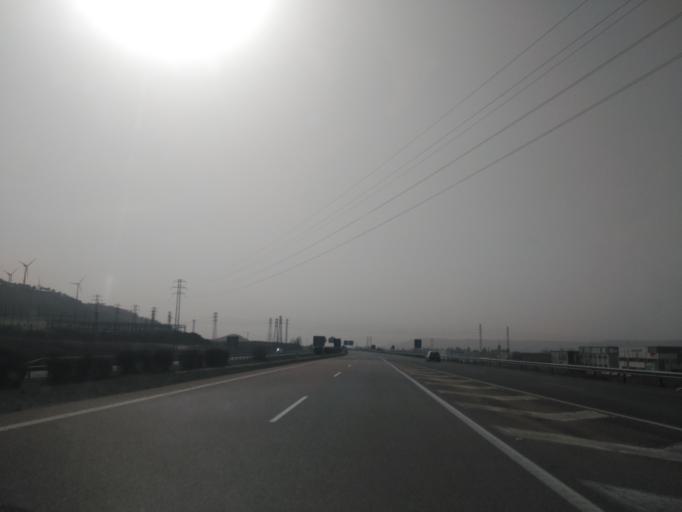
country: ES
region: Castille and Leon
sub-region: Provincia de Palencia
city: Palencia
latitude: 42.0031
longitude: -4.5014
